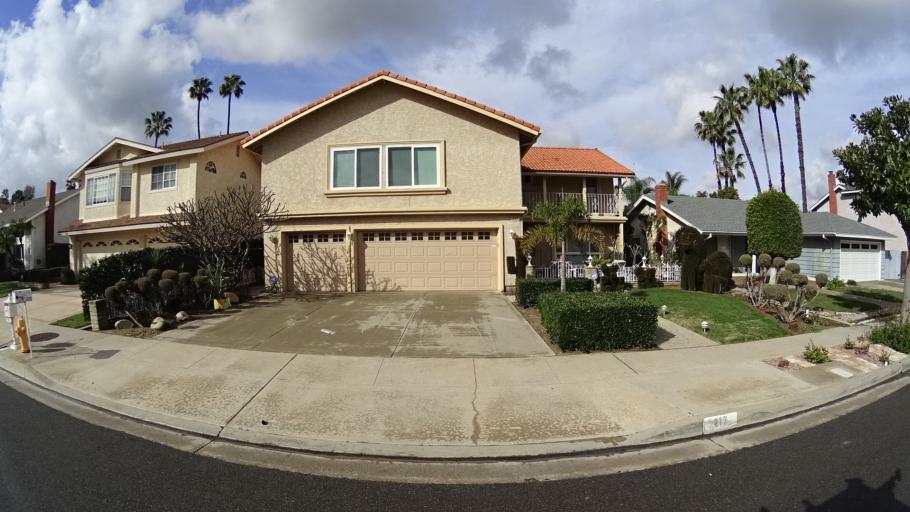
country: US
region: California
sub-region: Orange County
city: Villa Park
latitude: 33.8494
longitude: -117.7822
